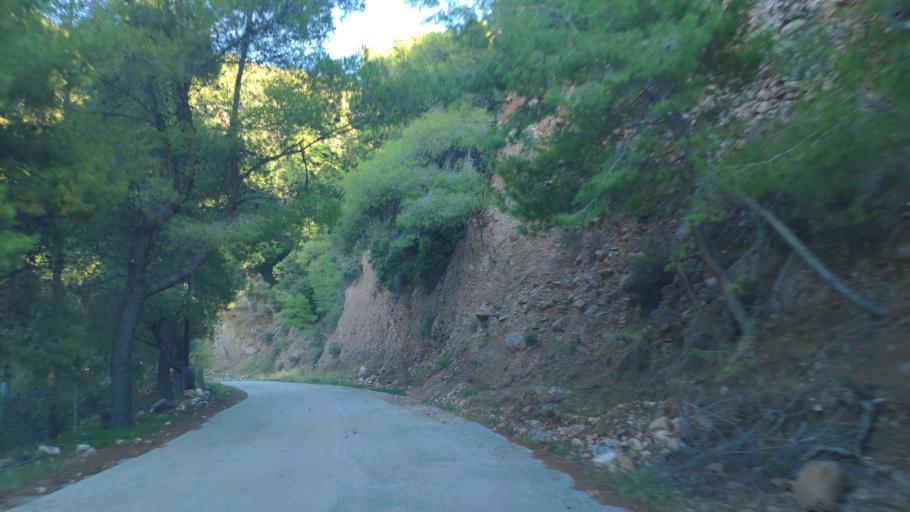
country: GR
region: Attica
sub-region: Nomos Piraios
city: Megalochori
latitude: 37.6052
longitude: 23.3308
